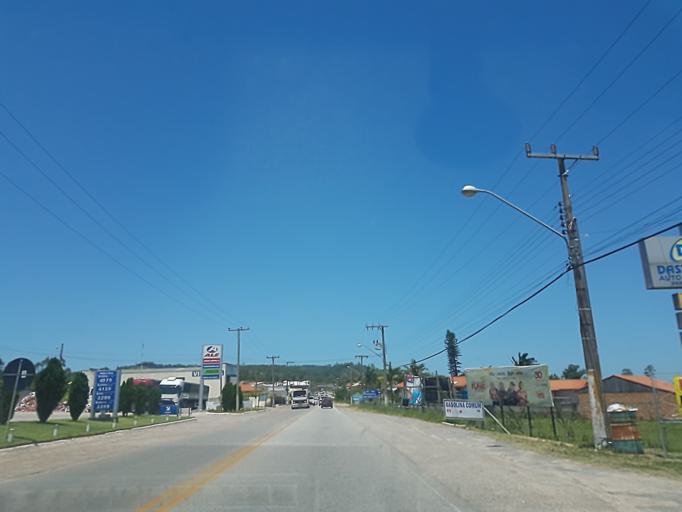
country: BR
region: Santa Catarina
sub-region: Jaguaruna
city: Jaguaruna
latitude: -28.6013
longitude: -49.0457
